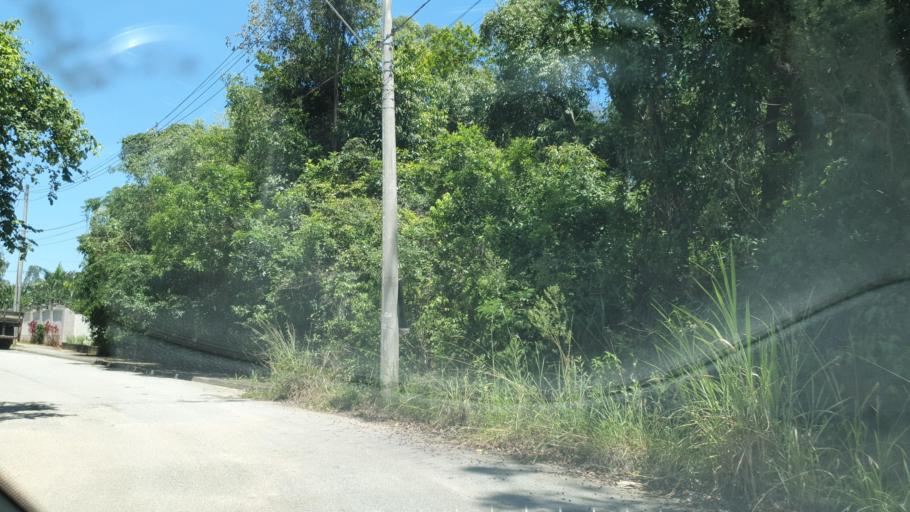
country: BR
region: Sao Paulo
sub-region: Sorocaba
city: Sorocaba
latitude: -23.4717
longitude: -47.4105
